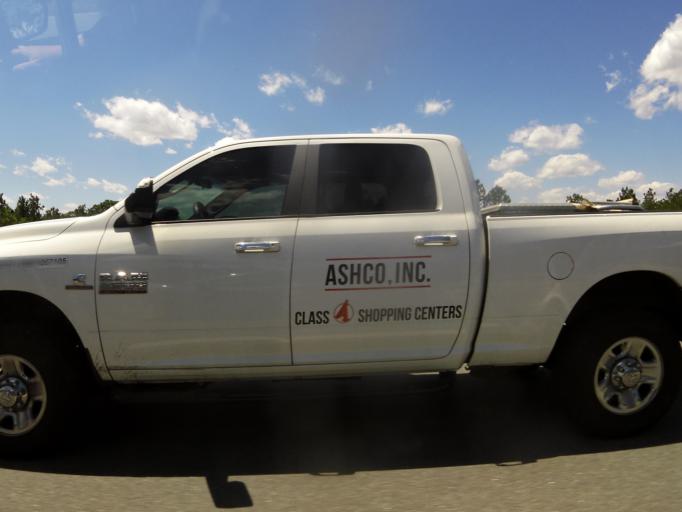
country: US
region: Florida
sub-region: Saint Johns County
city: Fruit Cove
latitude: 30.0103
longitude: -81.5062
